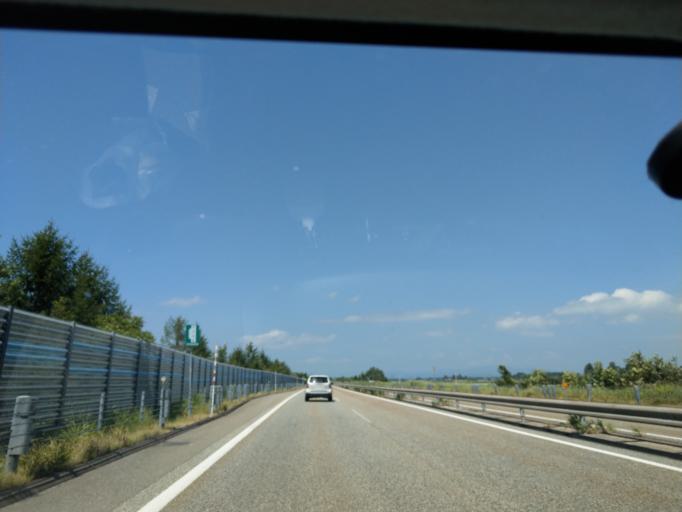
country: JP
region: Akita
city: Yokotemachi
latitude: 39.3627
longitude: 140.4882
